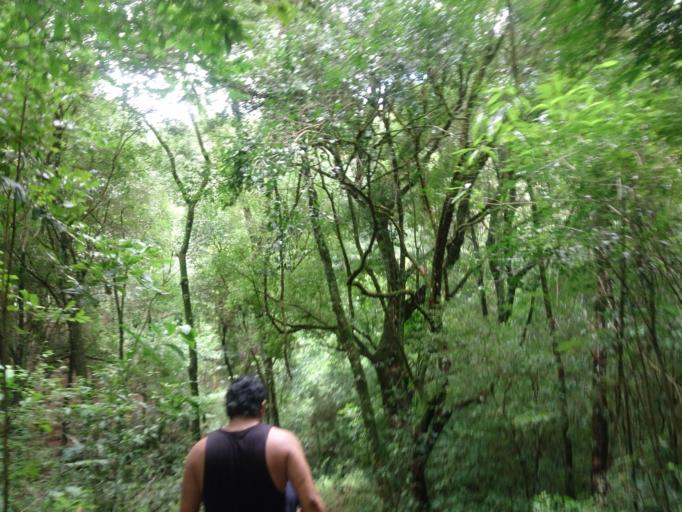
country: AR
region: Misiones
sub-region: Departamento de Obera
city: Obera
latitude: -27.5123
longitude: -55.1064
